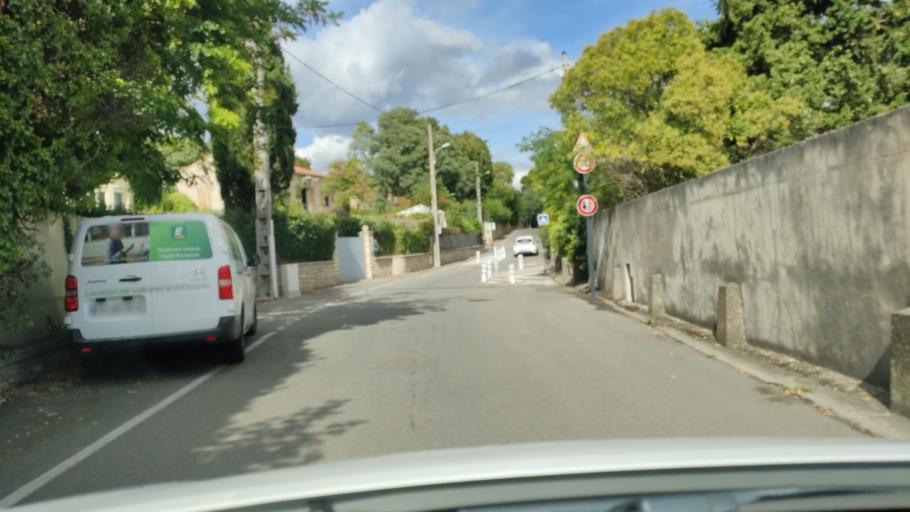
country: FR
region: Languedoc-Roussillon
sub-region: Departement du Gard
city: Villeneuve-les-Avignon
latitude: 43.9551
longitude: 4.7879
